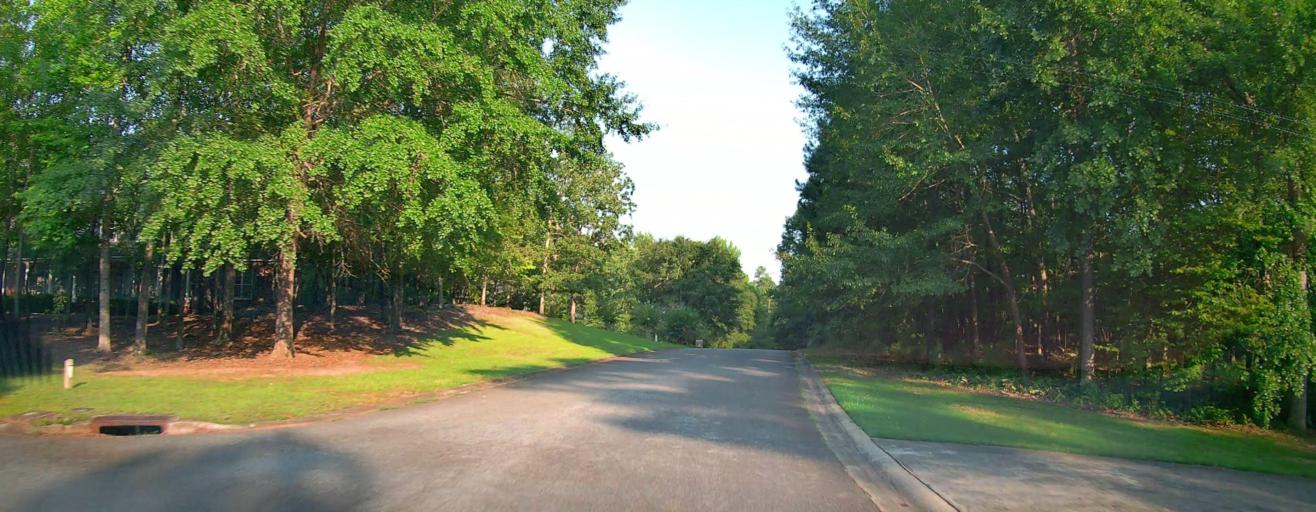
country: US
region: Georgia
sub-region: Bibb County
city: West Point
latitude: 32.8847
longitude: -83.8050
